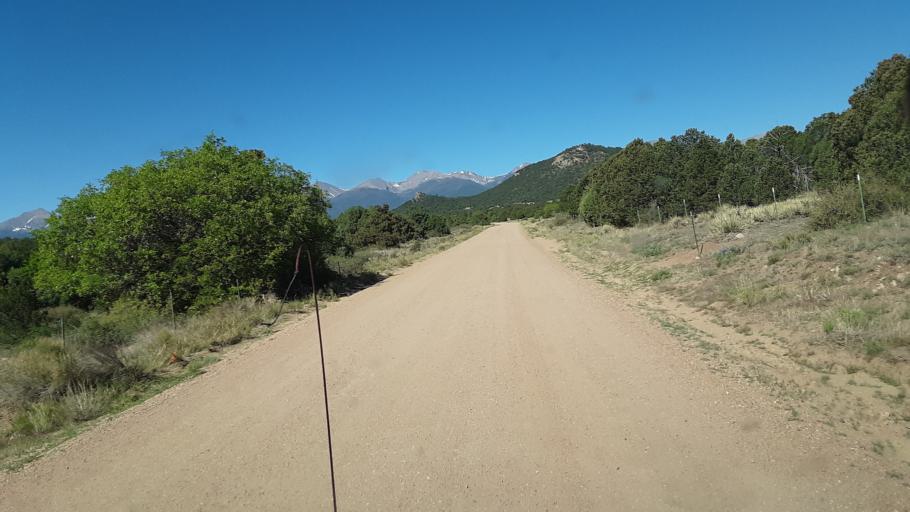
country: US
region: Colorado
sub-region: Custer County
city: Westcliffe
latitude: 38.2725
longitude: -105.5396
